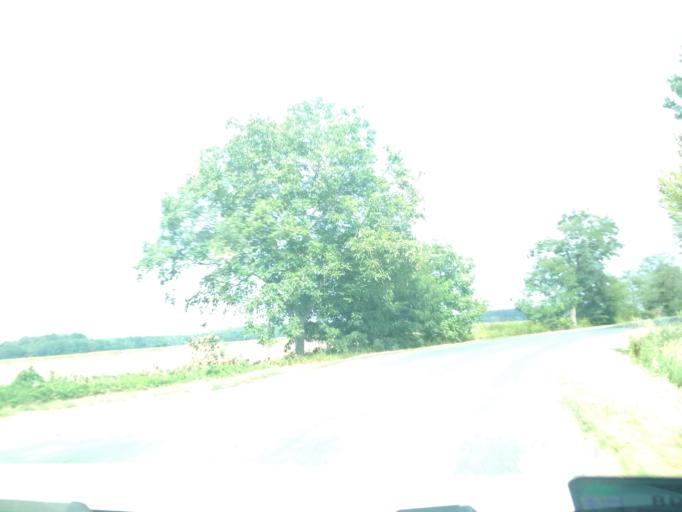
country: HU
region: Jasz-Nagykun-Szolnok
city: Tiszaszolos
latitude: 47.5244
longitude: 20.6700
